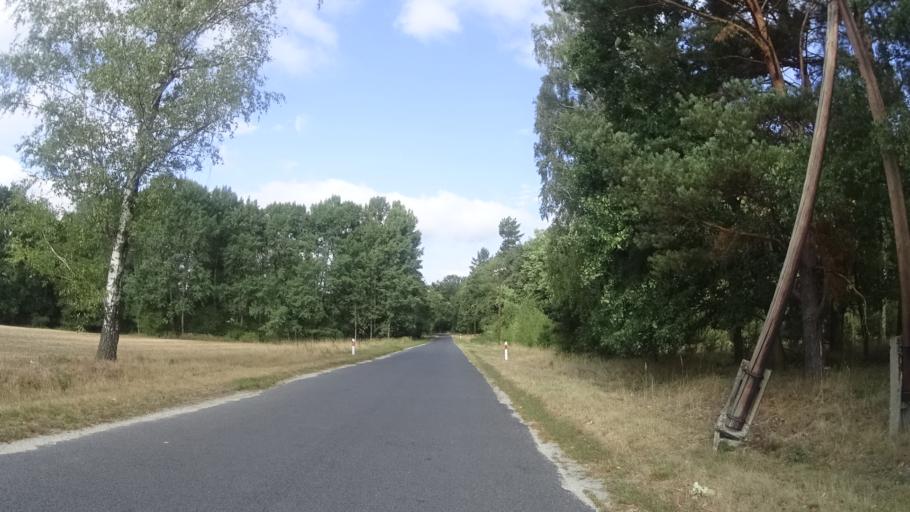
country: PL
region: Lubusz
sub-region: Powiat zarski
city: Przewoz
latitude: 51.4911
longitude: 14.8759
